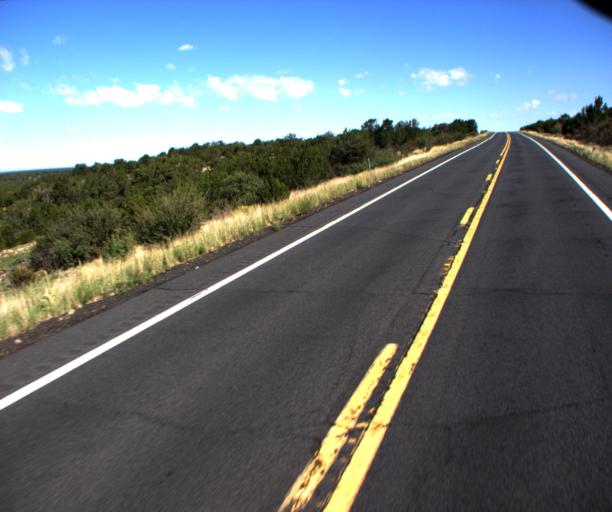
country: US
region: Arizona
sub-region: Coconino County
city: Williams
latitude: 35.4701
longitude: -112.1747
